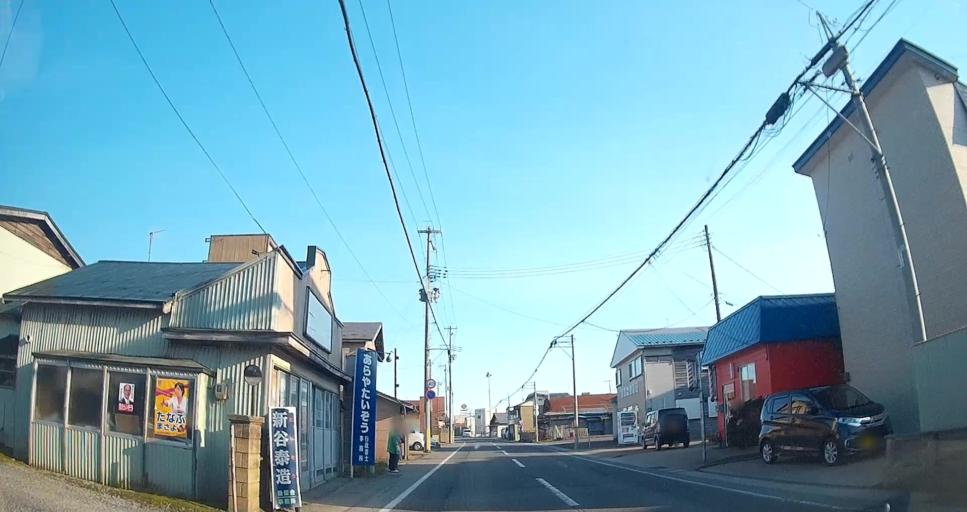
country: JP
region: Aomori
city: Mutsu
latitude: 41.2907
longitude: 141.2109
